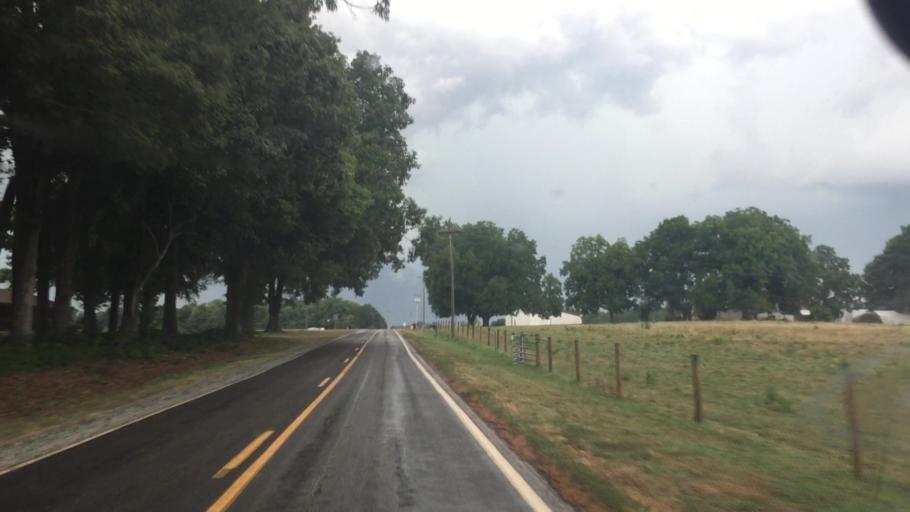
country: US
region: North Carolina
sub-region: Rowan County
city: Enochville
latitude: 35.6393
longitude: -80.6687
